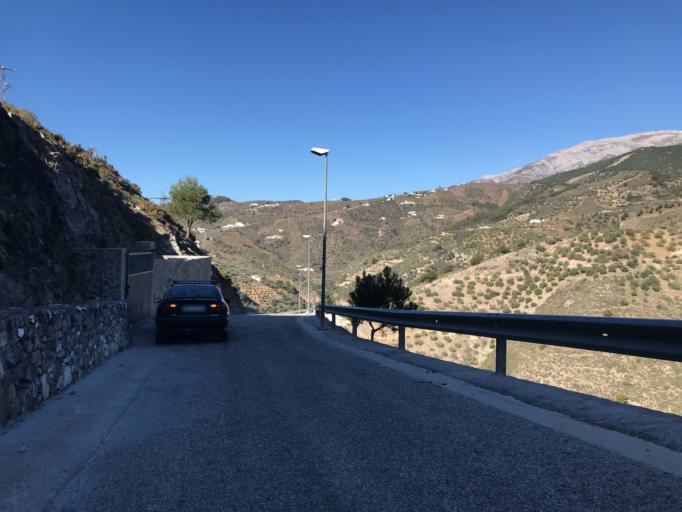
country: ES
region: Andalusia
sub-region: Provincia de Malaga
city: Canillas de Albaida
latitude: 36.8477
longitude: -3.9861
